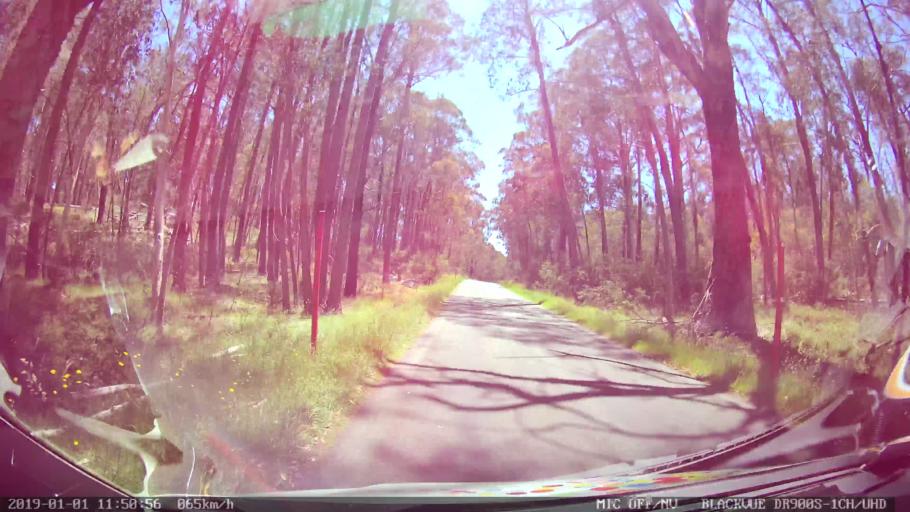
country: AU
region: New South Wales
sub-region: Snowy River
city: Jindabyne
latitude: -35.8886
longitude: 148.4257
